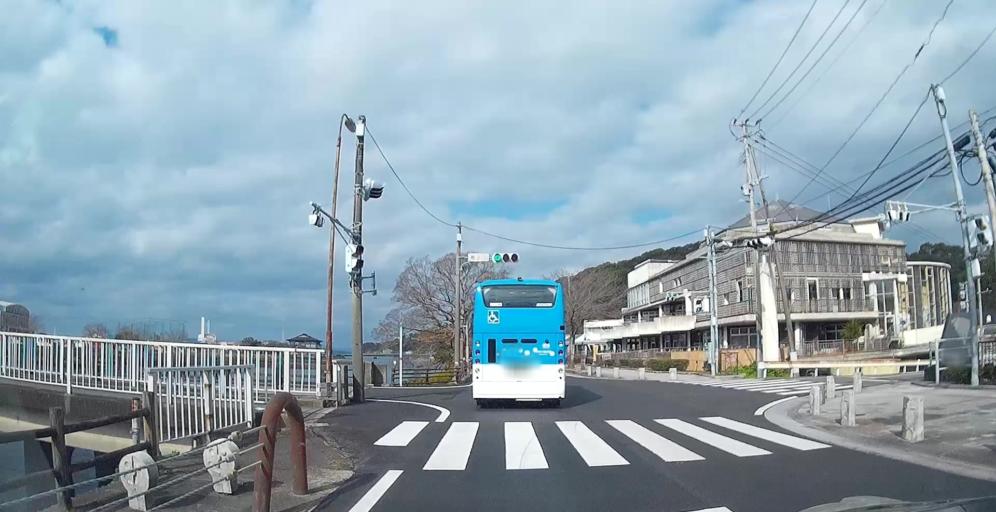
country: JP
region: Kumamoto
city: Minamata
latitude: 32.2144
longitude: 130.4070
